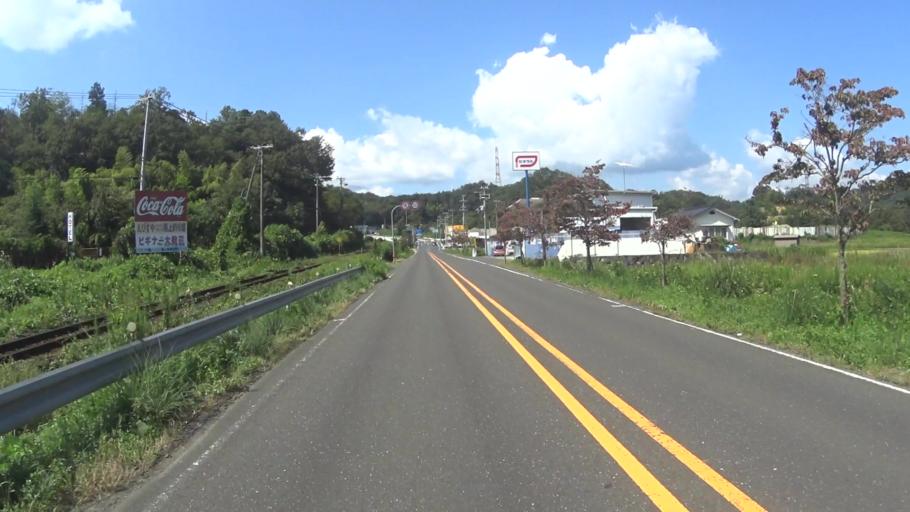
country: JP
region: Kyoto
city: Miyazu
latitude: 35.5495
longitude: 135.2306
